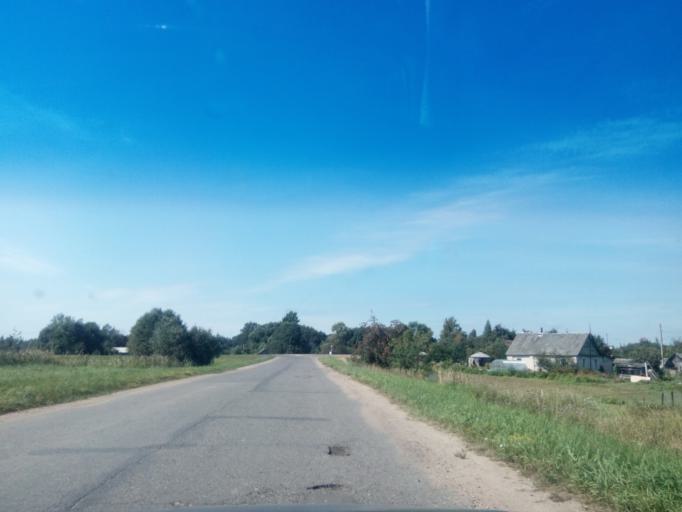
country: BY
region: Vitebsk
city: Vyerkhnyadzvinsk
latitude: 55.8366
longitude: 27.7326
